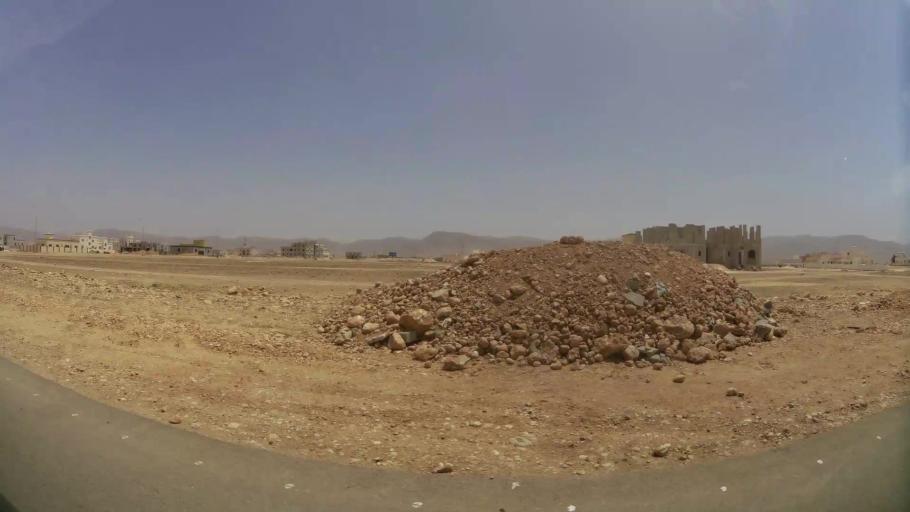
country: OM
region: Zufar
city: Salalah
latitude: 17.0979
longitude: 54.1933
